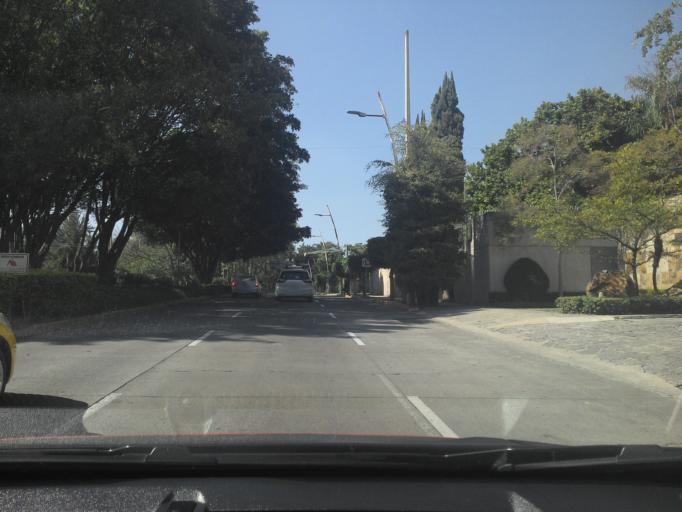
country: MX
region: Jalisco
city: Zapopan2
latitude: 20.6959
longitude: -103.3957
